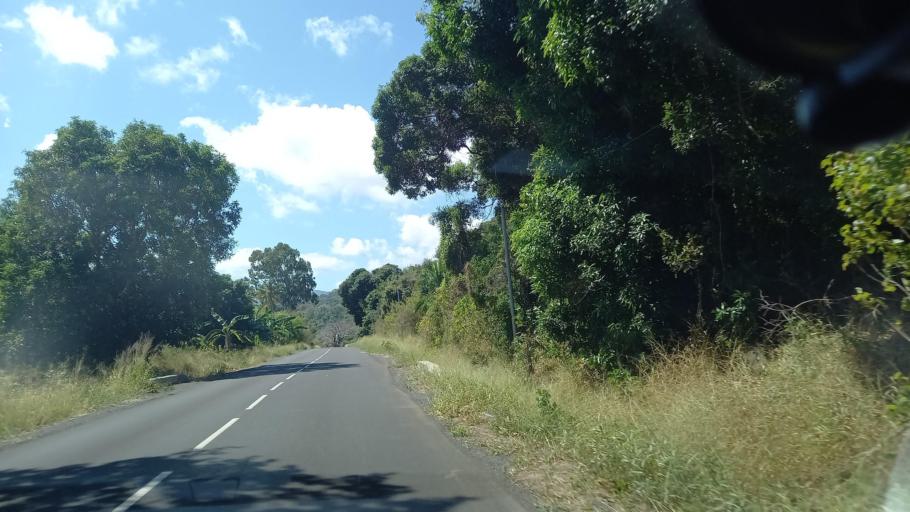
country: YT
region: Kani-Keli
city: Kani Keli
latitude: -12.9500
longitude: 45.0983
